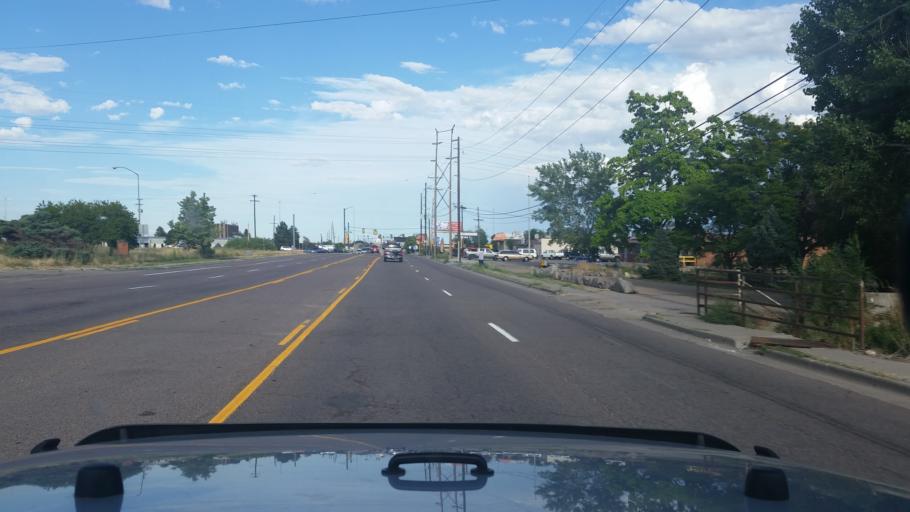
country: US
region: Colorado
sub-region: Adams County
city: Twin Lakes
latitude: 39.8235
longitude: -104.9900
